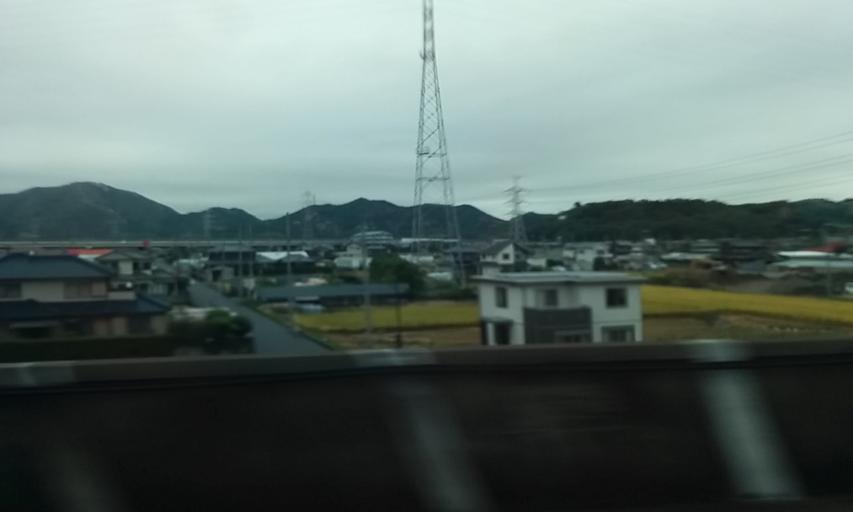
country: JP
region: Hyogo
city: Kakogawacho-honmachi
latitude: 34.7819
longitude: 134.7784
